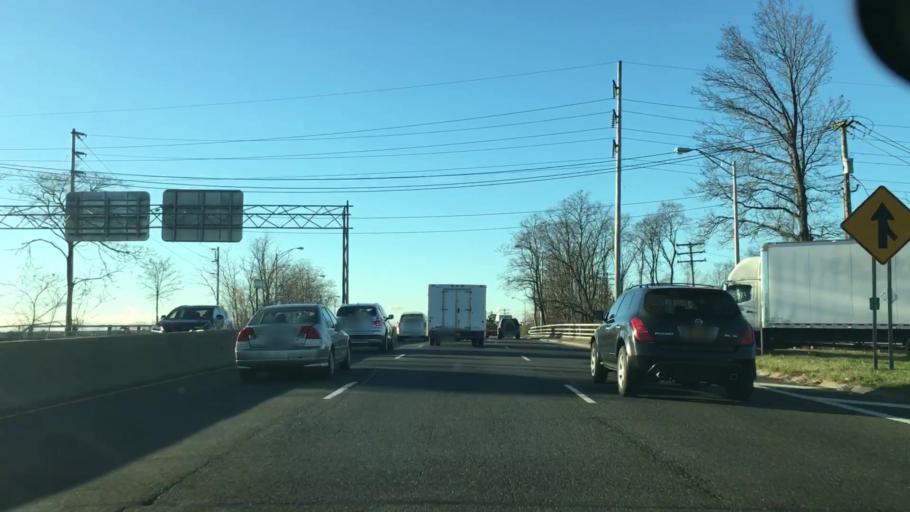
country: US
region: New York
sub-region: Suffolk County
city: East Farmingdale
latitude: 40.7221
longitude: -73.4253
